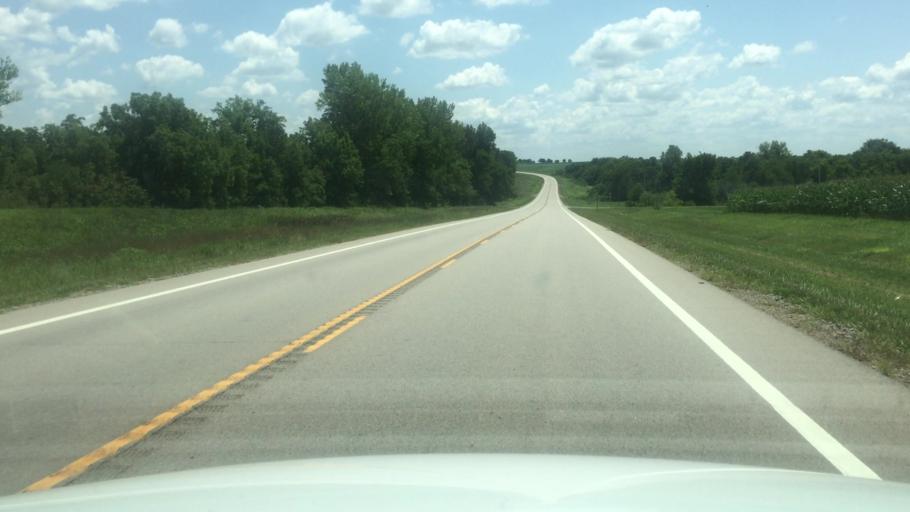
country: US
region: Kansas
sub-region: Brown County
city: Horton
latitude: 39.6255
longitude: -95.3505
